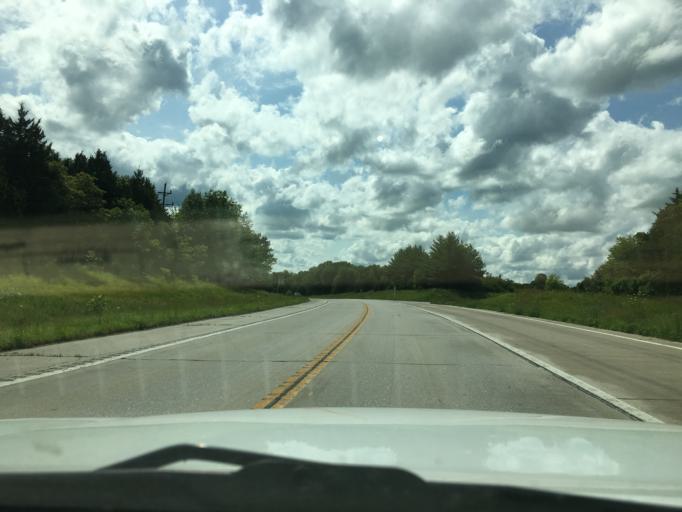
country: US
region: Missouri
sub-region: Franklin County
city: Gerald
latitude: 38.4232
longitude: -91.2615
